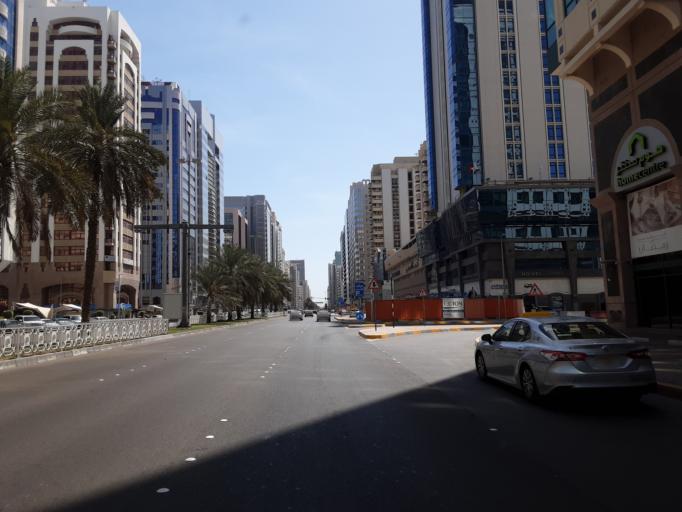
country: AE
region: Abu Dhabi
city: Abu Dhabi
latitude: 24.4882
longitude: 54.3612
